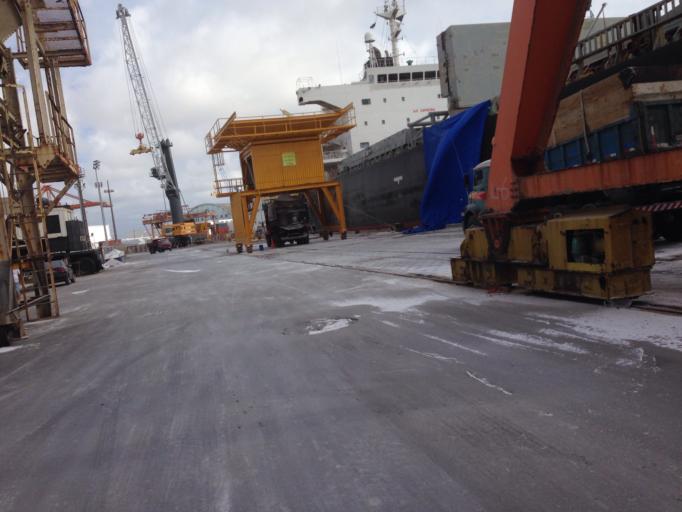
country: BR
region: Pernambuco
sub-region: Recife
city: Recife
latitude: -8.0513
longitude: -34.8683
